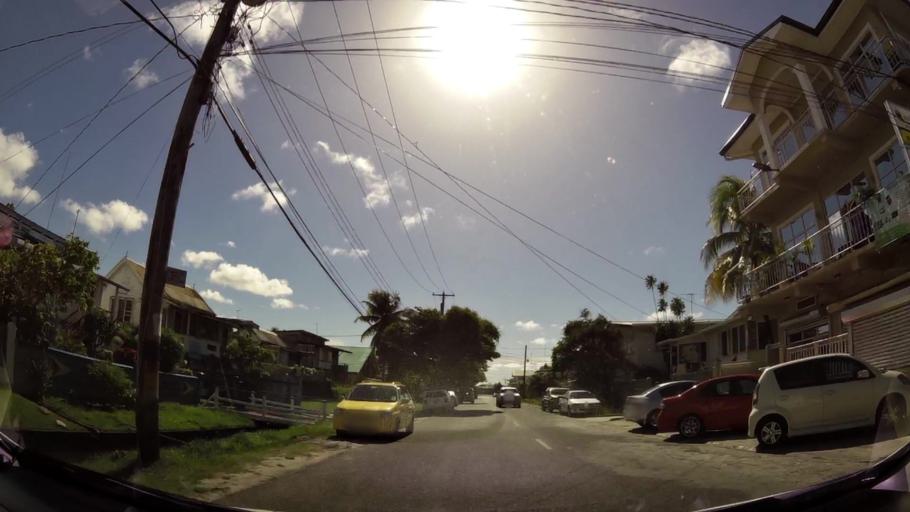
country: GY
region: Demerara-Mahaica
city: Georgetown
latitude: 6.8227
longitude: -58.1420
